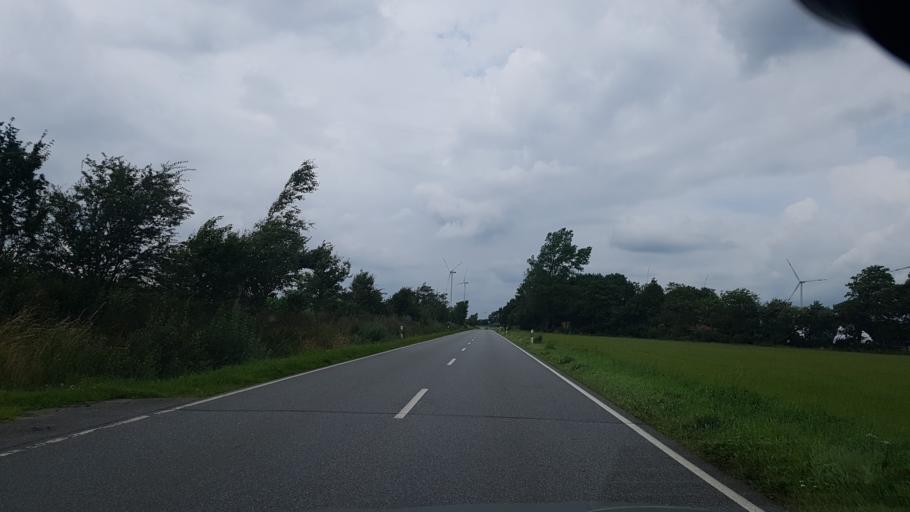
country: DE
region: Schleswig-Holstein
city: Jardelund
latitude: 54.8360
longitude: 9.2133
